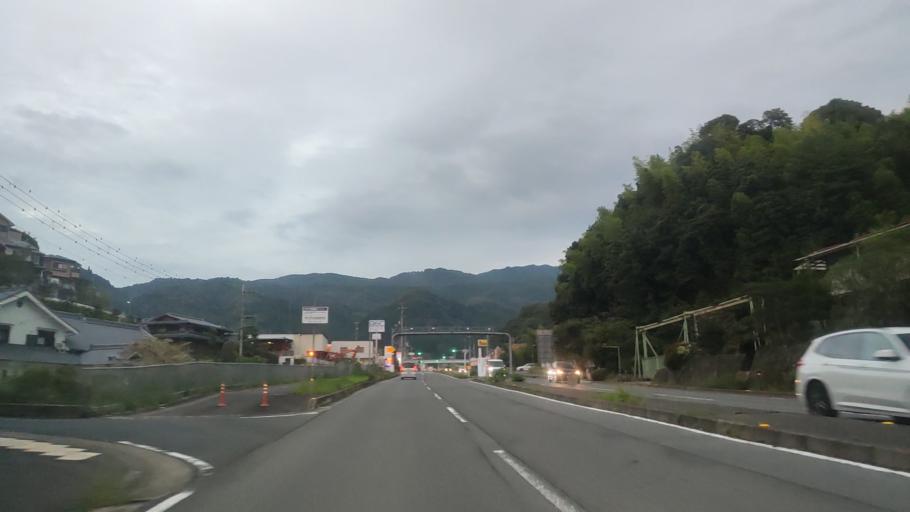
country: JP
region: Wakayama
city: Hashimoto
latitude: 34.3641
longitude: 135.6058
